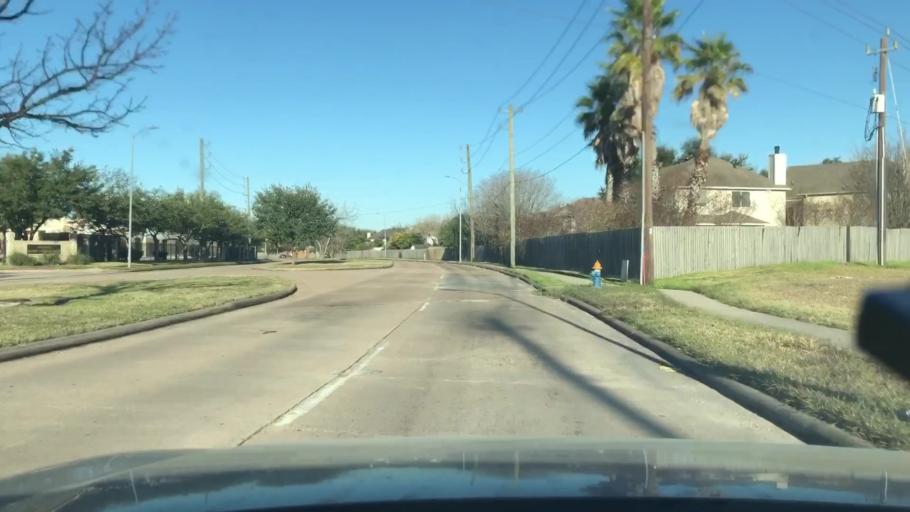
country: US
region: Texas
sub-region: Fort Bend County
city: Missouri City
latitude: 29.6438
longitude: -95.5306
